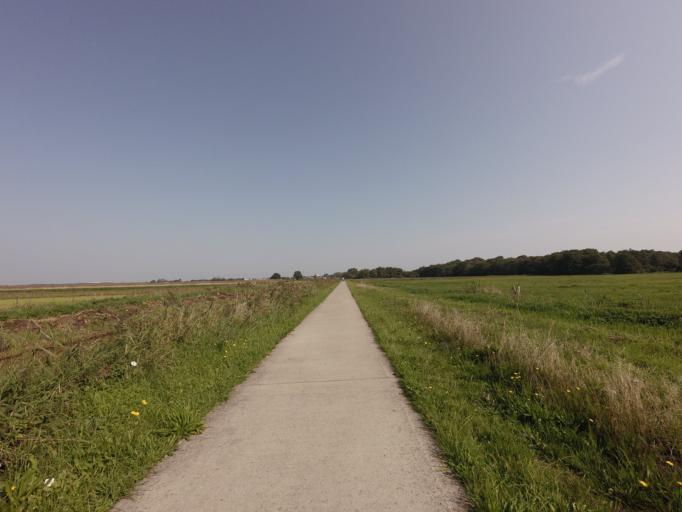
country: NL
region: Groningen
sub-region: Gemeente Groningen
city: Groningen
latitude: 53.1639
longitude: 6.5408
